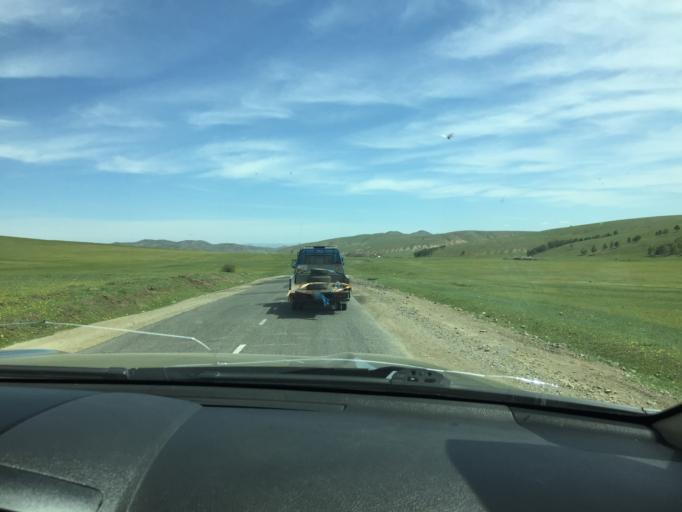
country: MN
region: Central Aimak
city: Javhlant
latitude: 48.6546
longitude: 106.1118
